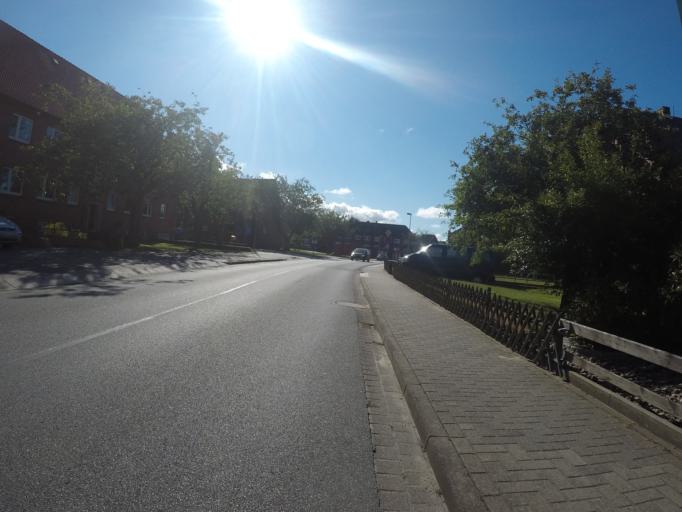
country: DE
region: Lower Saxony
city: Otterndorf
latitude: 53.8121
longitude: 8.9053
